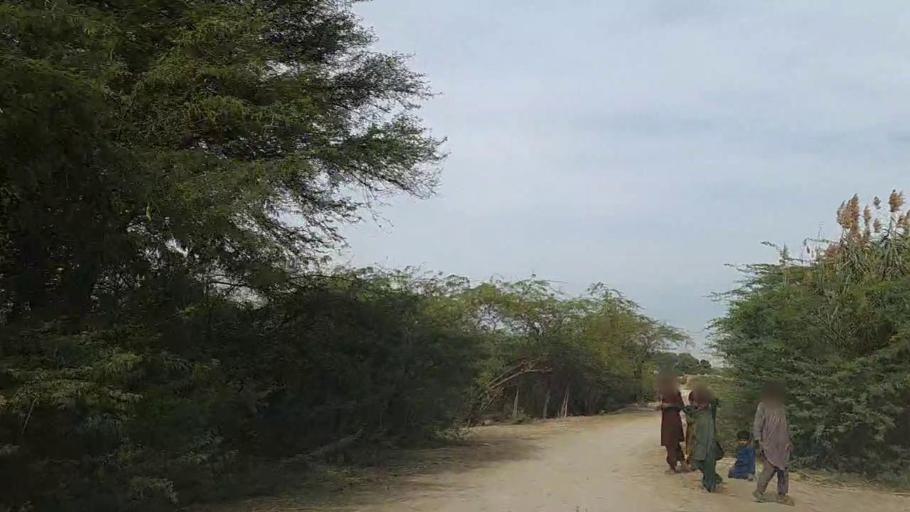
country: PK
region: Sindh
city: Daur
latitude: 26.4247
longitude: 68.4165
